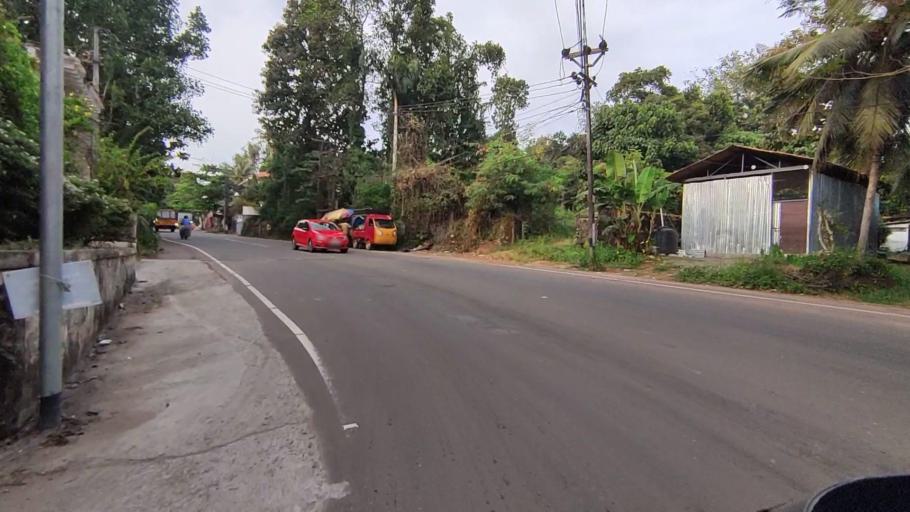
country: IN
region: Kerala
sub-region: Kottayam
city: Kottayam
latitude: 9.6183
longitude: 76.5104
